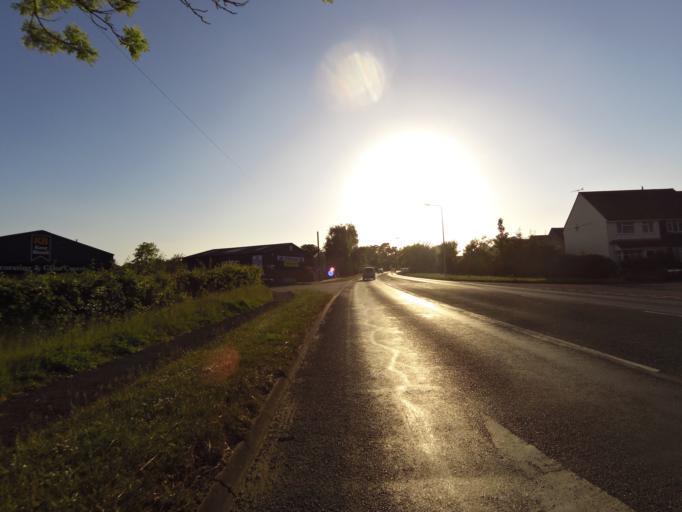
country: GB
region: England
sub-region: Suffolk
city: Woodbridge
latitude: 52.1042
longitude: 1.3333
